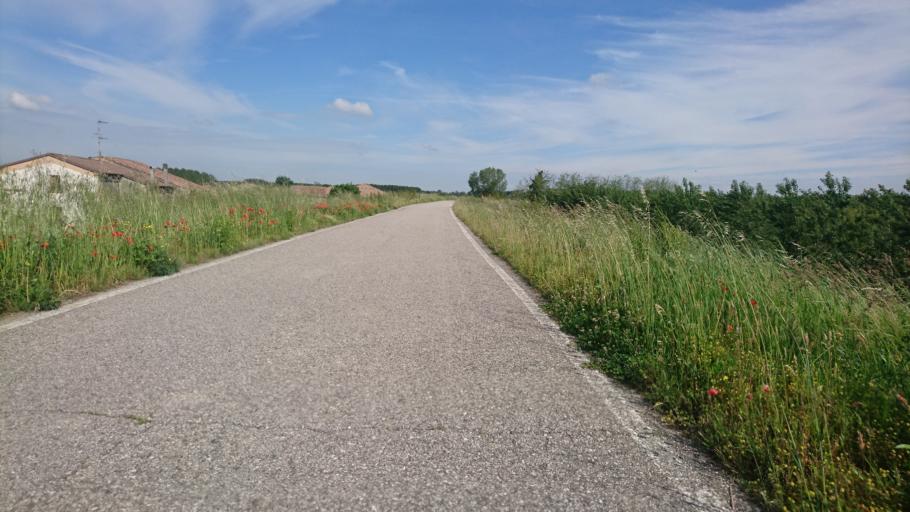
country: IT
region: Lombardy
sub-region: Provincia di Mantova
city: Borgofranco sul Po
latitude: 45.0432
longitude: 11.2167
